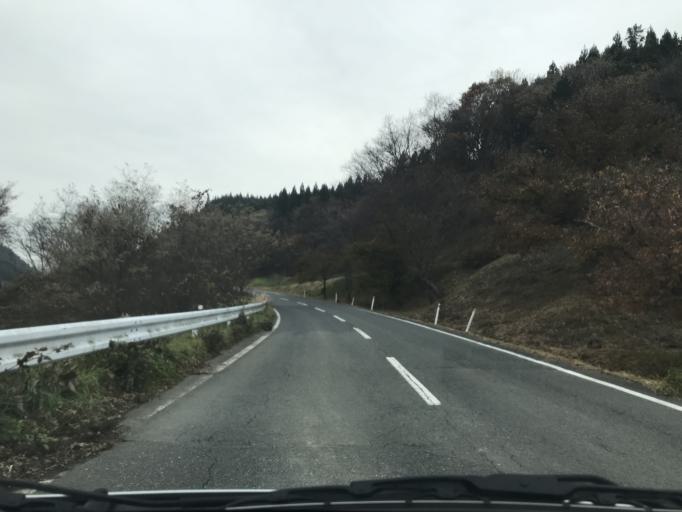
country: JP
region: Iwate
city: Kitakami
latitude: 39.2644
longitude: 141.1828
